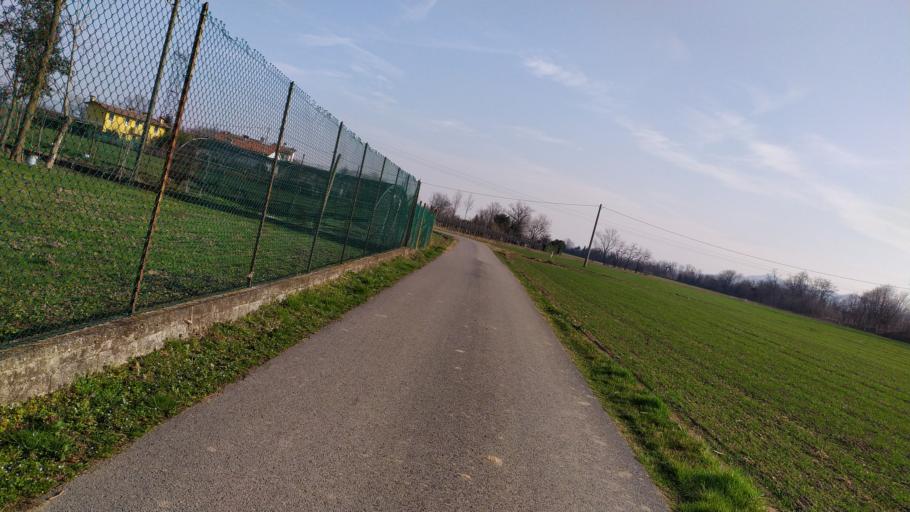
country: IT
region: Veneto
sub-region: Provincia di Vicenza
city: Giavenale
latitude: 45.6912
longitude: 11.4033
